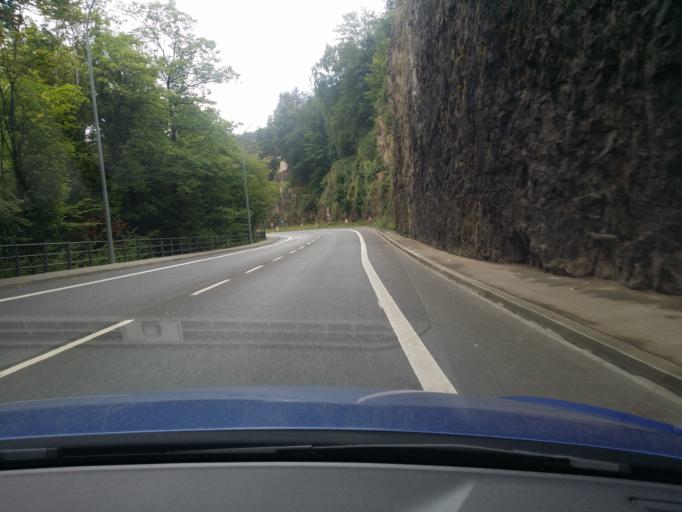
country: LU
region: Luxembourg
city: Kirchberg
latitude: 49.6083
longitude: 6.1461
